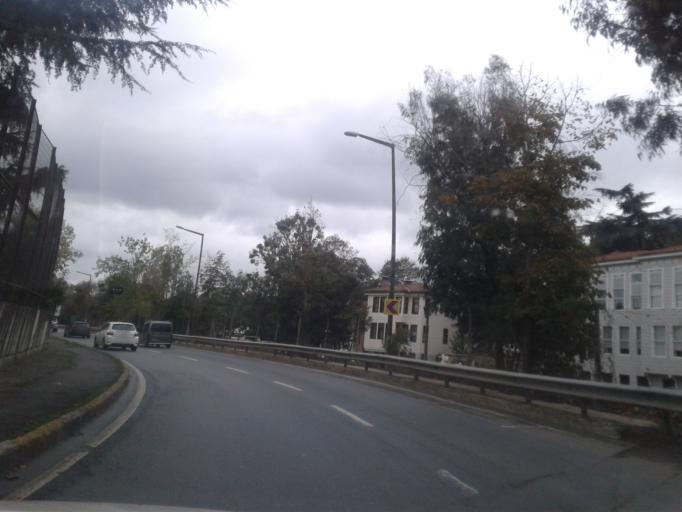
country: TR
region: Istanbul
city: UEskuedar
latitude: 41.0825
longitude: 29.0712
